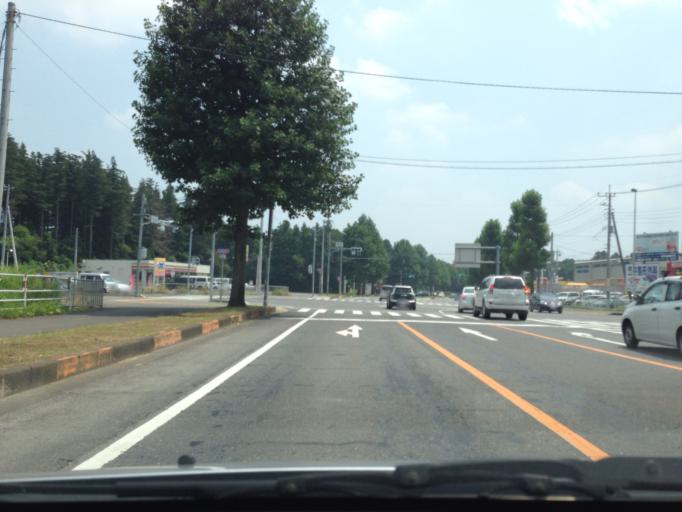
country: JP
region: Ibaraki
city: Naka
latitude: 36.0358
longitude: 140.1390
